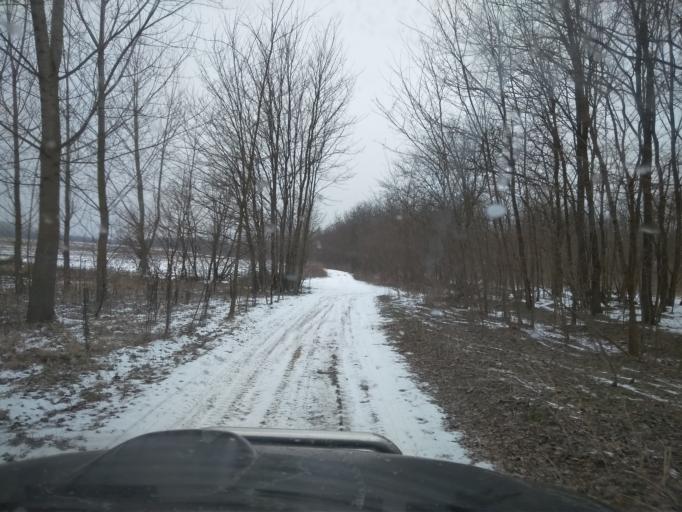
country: HU
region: Szabolcs-Szatmar-Bereg
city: Apagy
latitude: 47.9801
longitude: 21.9124
